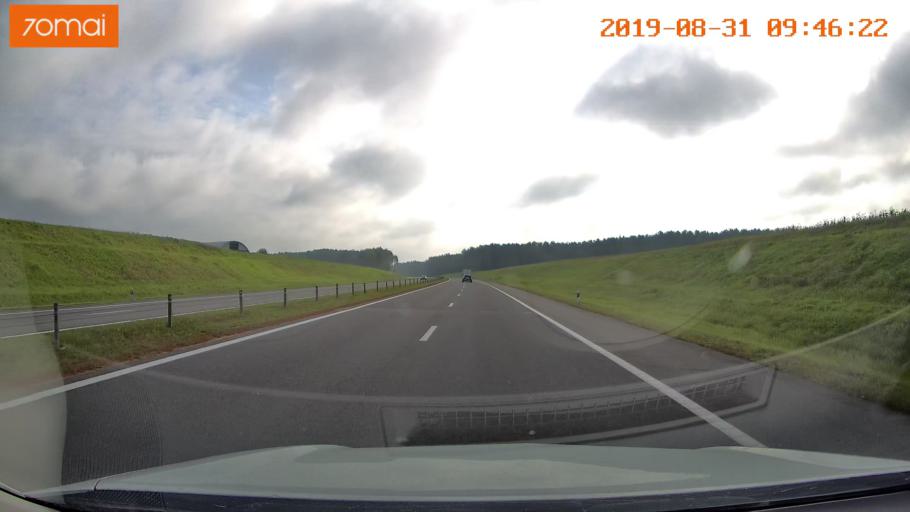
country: BY
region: Mogilev
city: Byalynichy
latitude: 53.9397
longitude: 29.6042
